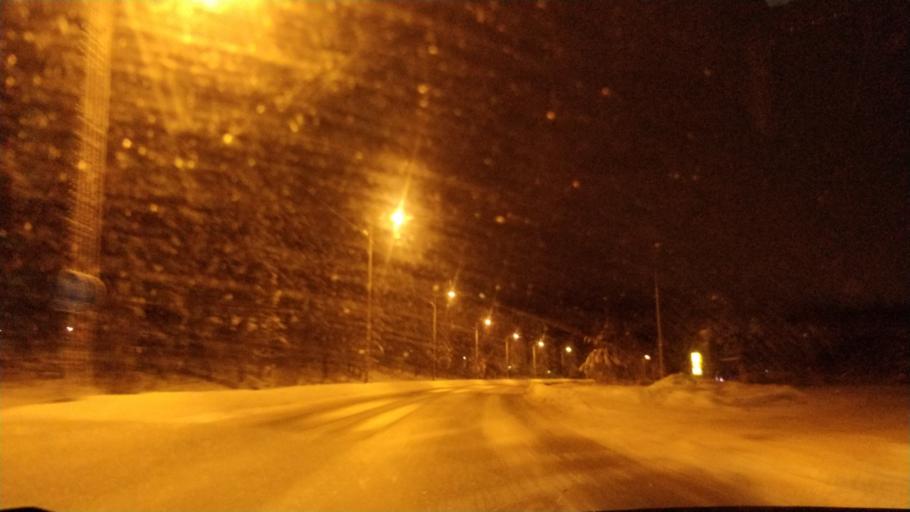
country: FI
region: Lapland
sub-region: Rovaniemi
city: Rovaniemi
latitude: 66.3763
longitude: 25.3832
